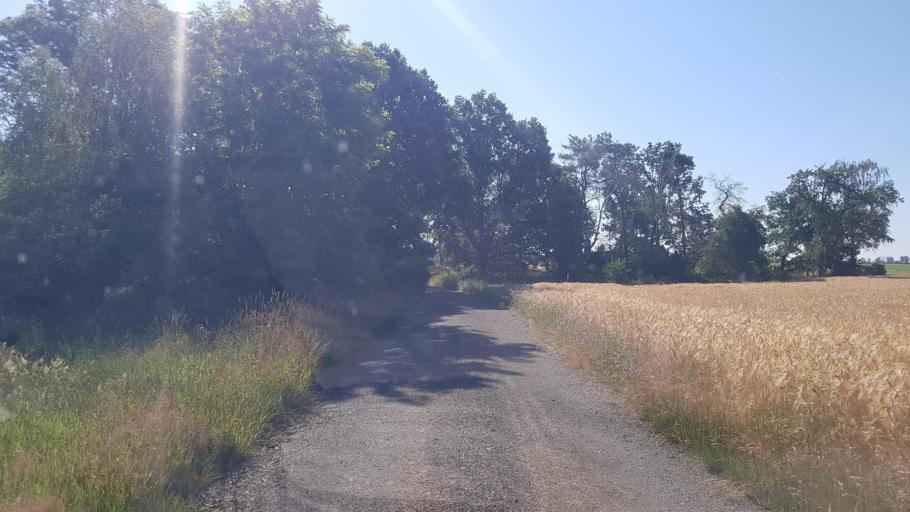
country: DE
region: Brandenburg
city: Juterbog
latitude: 51.9477
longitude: 13.2040
